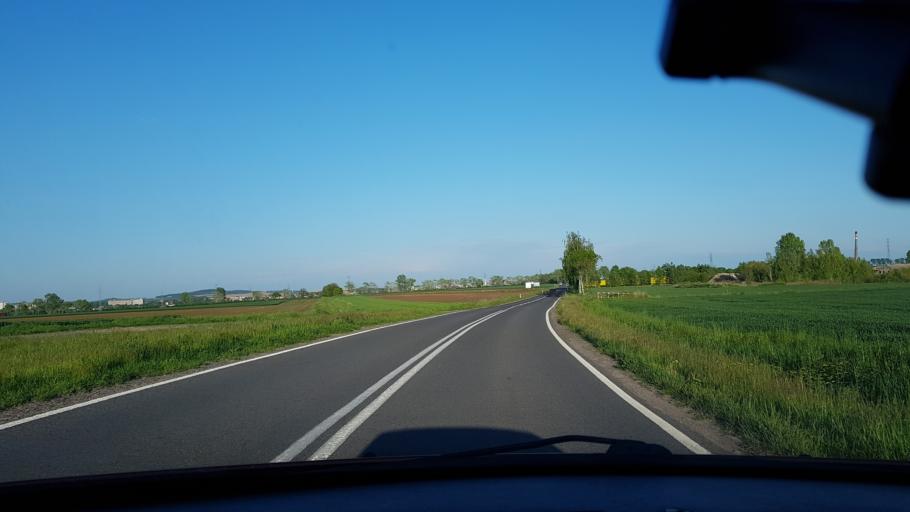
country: PL
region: Lower Silesian Voivodeship
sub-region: Powiat zabkowicki
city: Stoszowice
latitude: 50.5975
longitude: 16.7734
